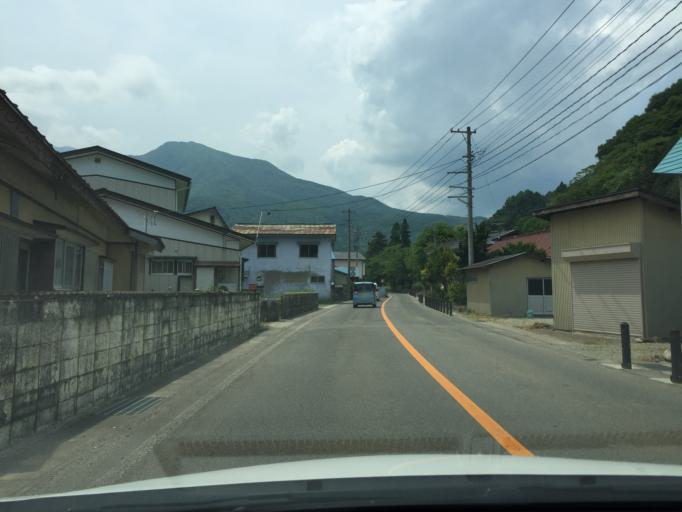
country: JP
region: Fukushima
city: Inawashiro
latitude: 37.6071
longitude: 140.1346
